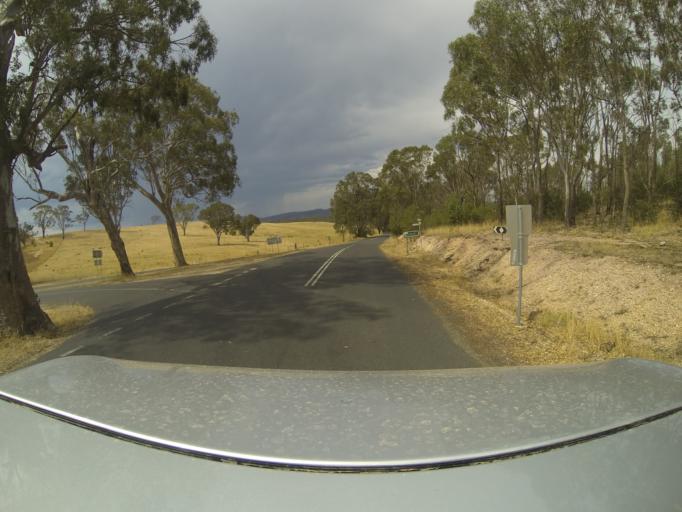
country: AU
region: Victoria
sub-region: Wellington
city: Heyfield
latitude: -37.8994
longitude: 146.7275
